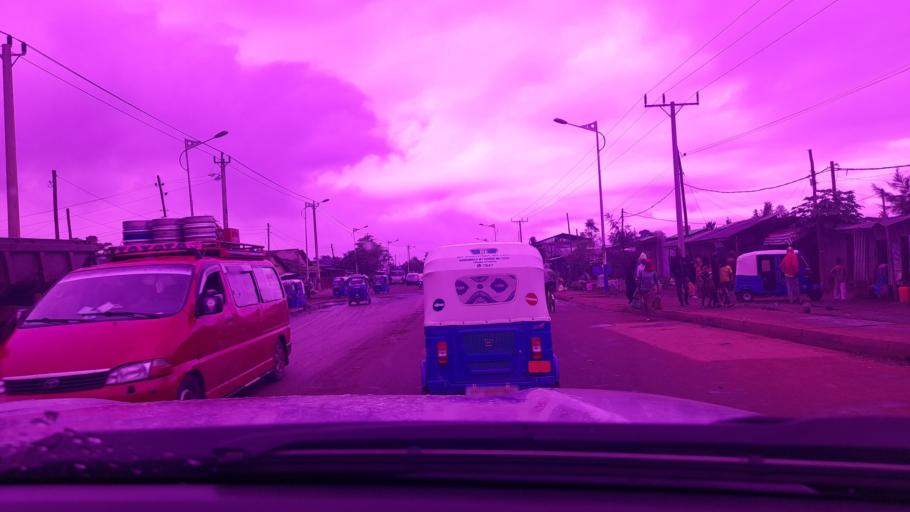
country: ET
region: Oromiya
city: Jima
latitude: 7.6627
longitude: 36.8416
